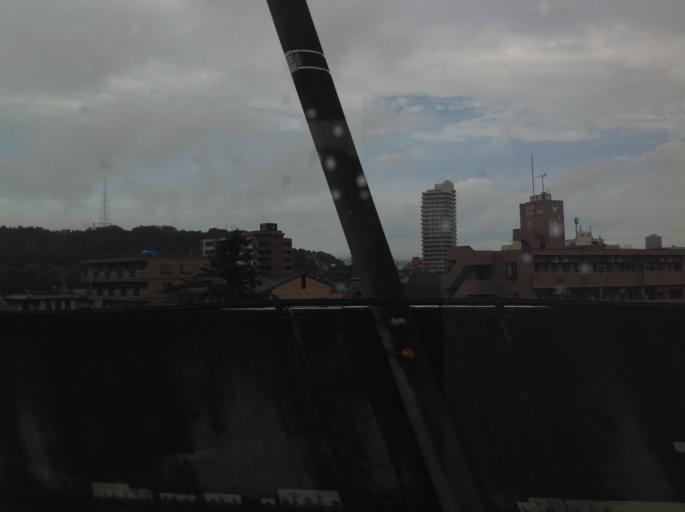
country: JP
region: Miyagi
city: Sendai
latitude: 38.2359
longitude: 140.8918
